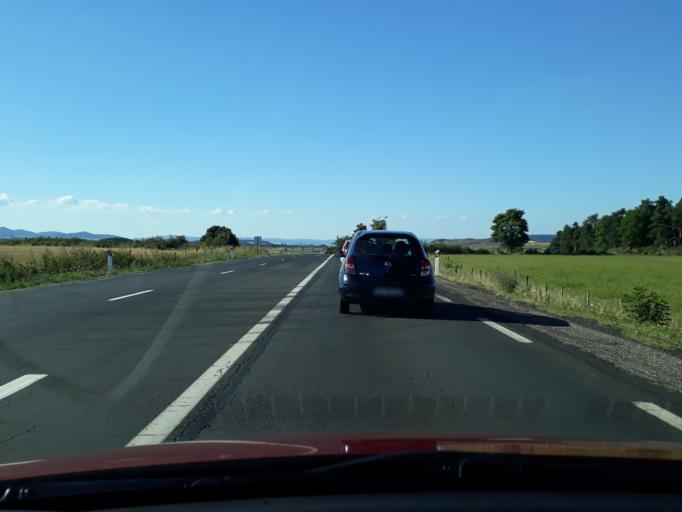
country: FR
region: Auvergne
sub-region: Departement de la Haute-Loire
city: Solignac-sur-Loire
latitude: 44.9118
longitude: 3.8488
